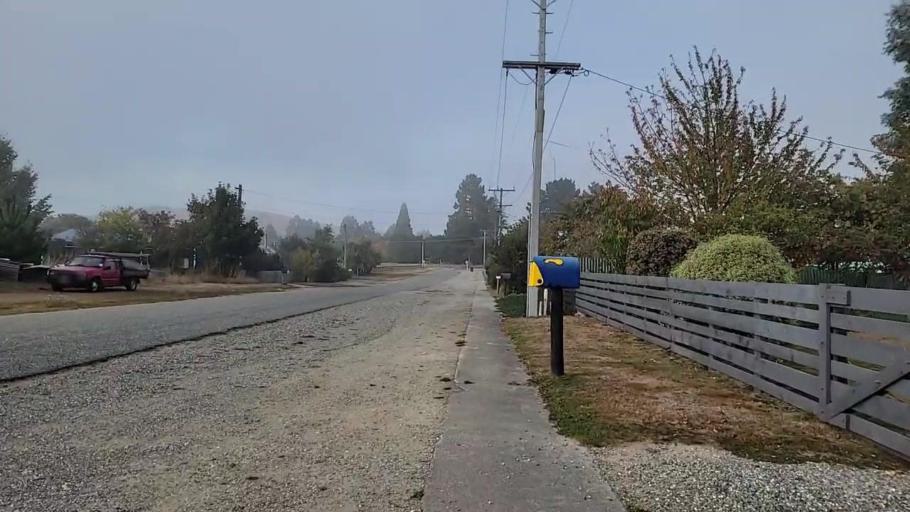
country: NZ
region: Southland
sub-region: Gore District
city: Gore
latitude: -45.6308
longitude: 169.3616
